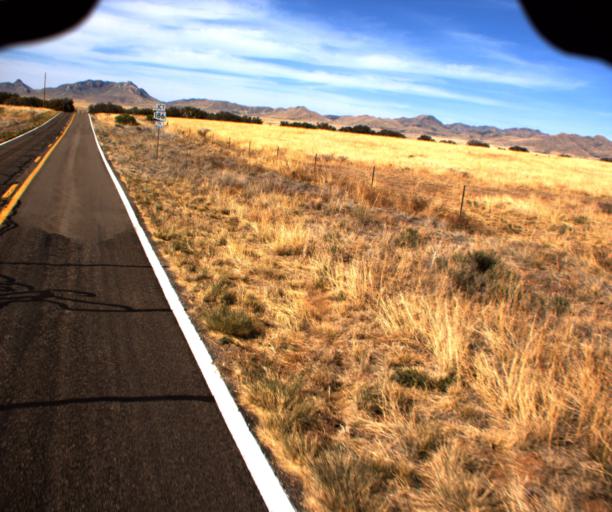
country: US
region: Arizona
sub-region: Cochise County
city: Willcox
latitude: 31.9980
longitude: -109.4400
